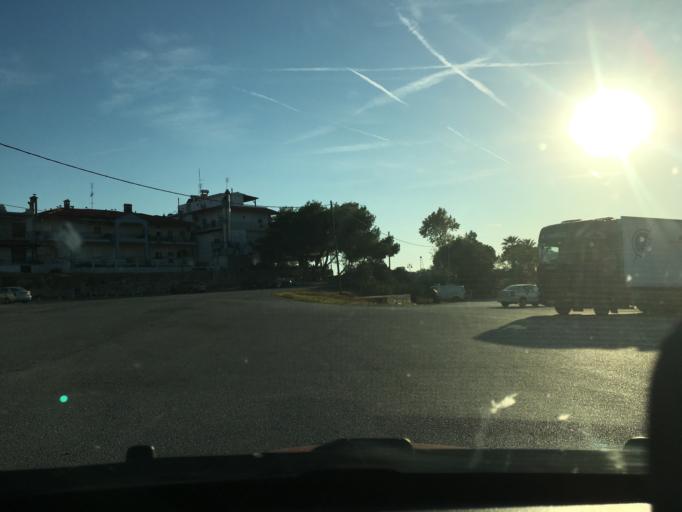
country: GR
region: Central Macedonia
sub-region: Nomos Chalkidikis
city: Nea Poteidaia
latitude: 40.1964
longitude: 23.3245
